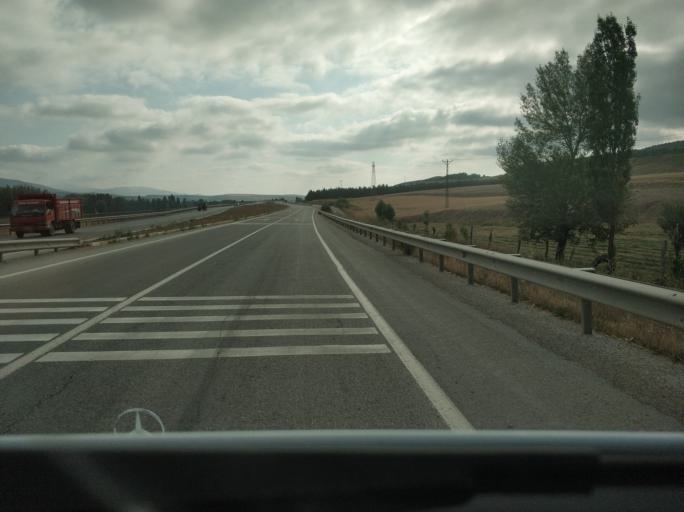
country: TR
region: Sivas
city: Yildizeli
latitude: 39.8624
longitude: 36.5704
